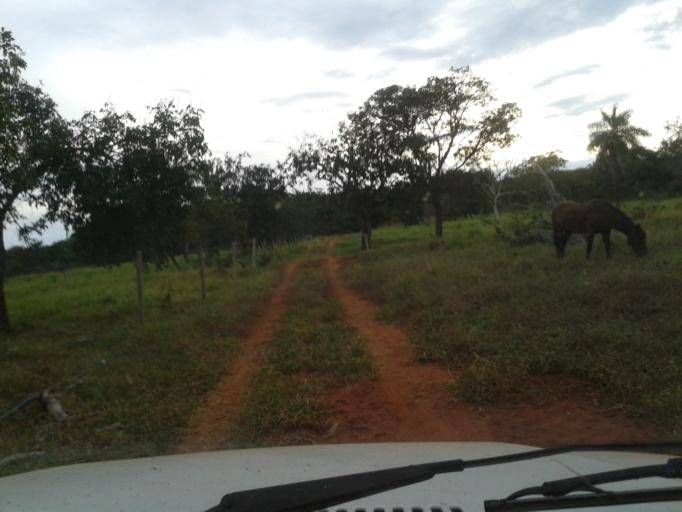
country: BR
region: Minas Gerais
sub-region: Campina Verde
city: Campina Verde
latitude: -19.4177
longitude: -49.6098
